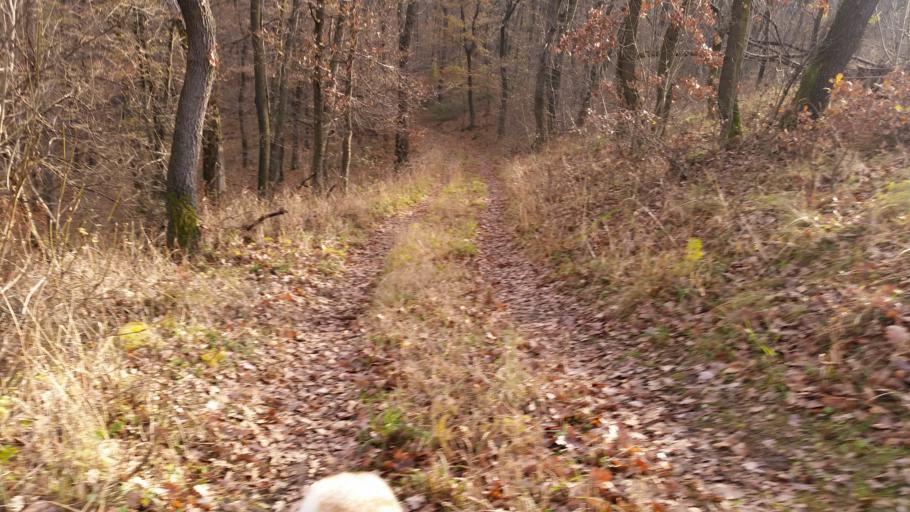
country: HU
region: Pest
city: Telki
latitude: 47.5748
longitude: 18.8238
